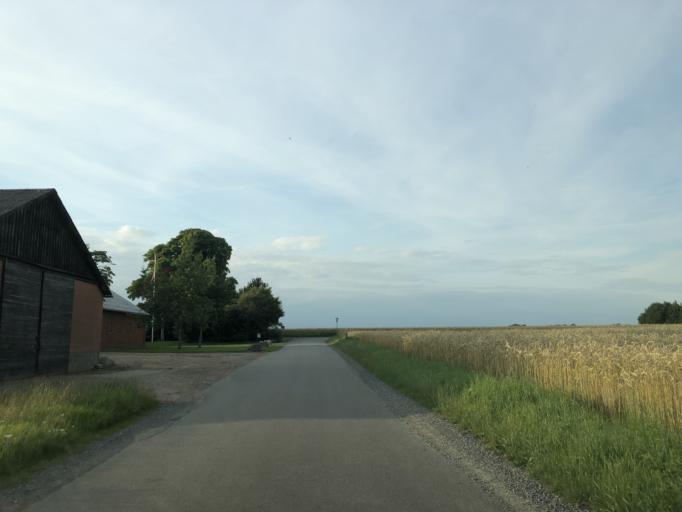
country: DK
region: South Denmark
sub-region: Vejle Kommune
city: Borkop
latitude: 55.6144
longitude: 9.6096
